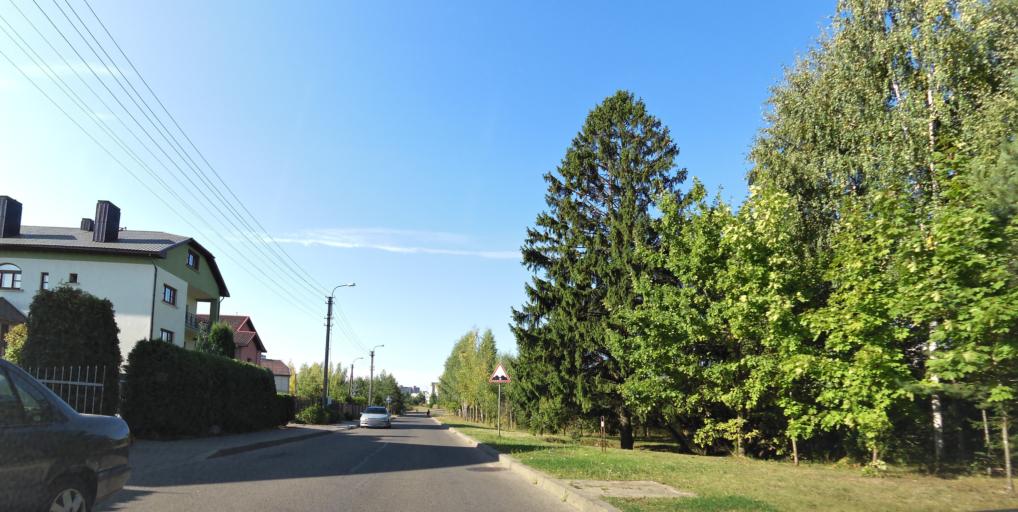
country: LT
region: Vilnius County
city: Pilaite
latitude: 54.7118
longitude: 25.1916
